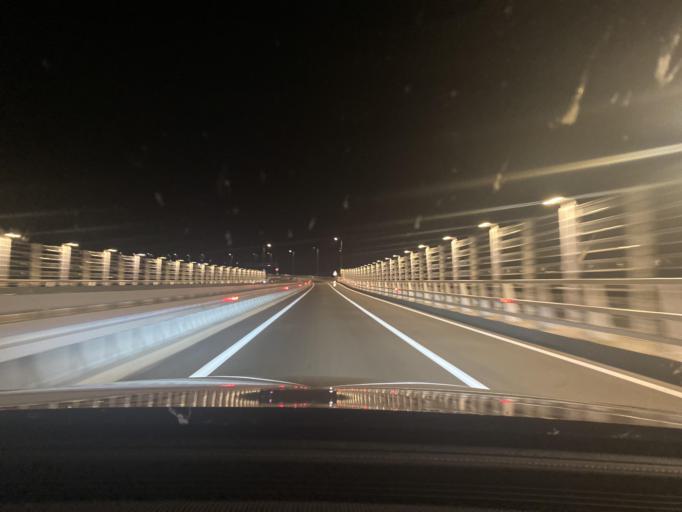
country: BA
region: Federation of Bosnia and Herzegovina
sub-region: Hercegovacko-Bosanski Kanton
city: Neum
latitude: 42.9245
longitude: 17.5289
